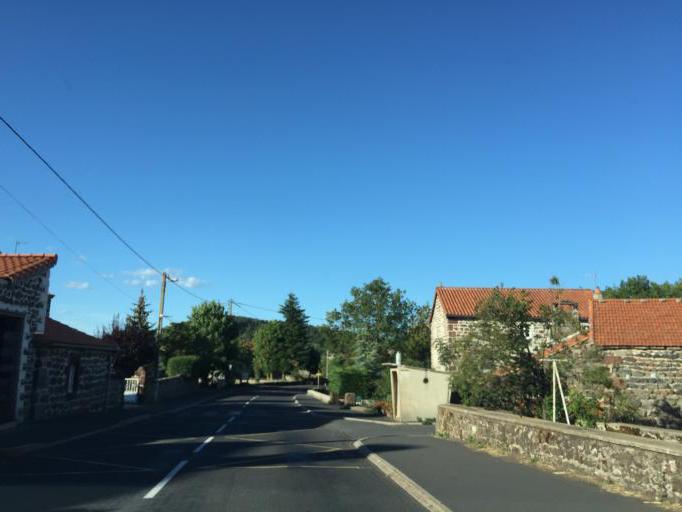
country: FR
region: Auvergne
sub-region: Departement de la Haute-Loire
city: Bains
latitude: 44.9904
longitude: 3.7424
